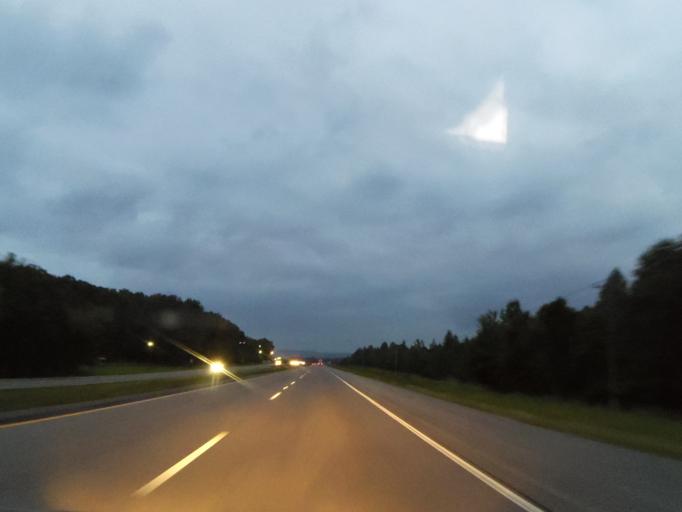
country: US
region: Alabama
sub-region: Madison County
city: New Hope
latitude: 34.6219
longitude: -86.3026
